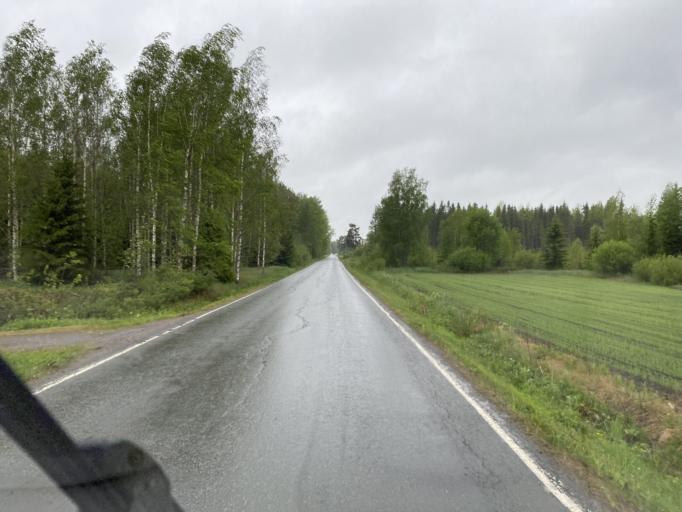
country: FI
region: Pirkanmaa
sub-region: Etelae-Pirkanmaa
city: Urjala
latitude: 60.9676
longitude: 23.5240
